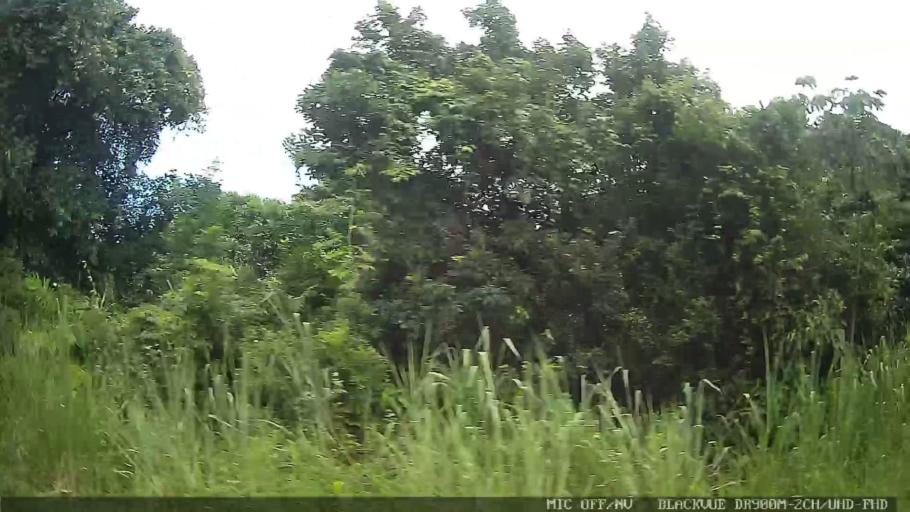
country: BR
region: Sao Paulo
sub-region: Iguape
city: Iguape
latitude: -24.6617
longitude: -47.4175
